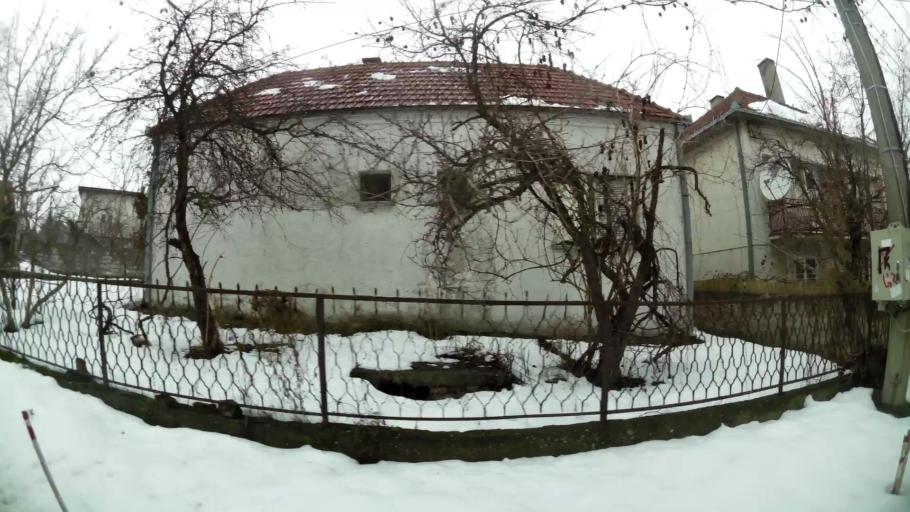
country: RS
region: Central Serbia
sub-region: Belgrade
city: Zvezdara
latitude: 44.7603
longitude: 20.5197
